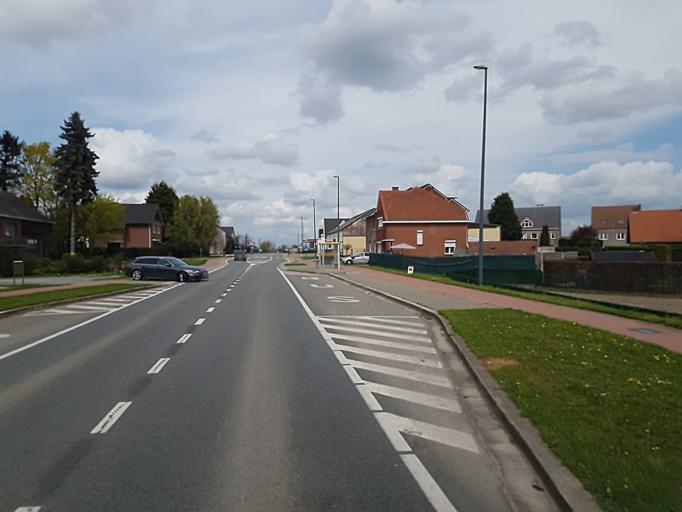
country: BE
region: Flanders
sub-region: Provincie Limburg
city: Lanaken
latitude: 50.8689
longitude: 5.6250
